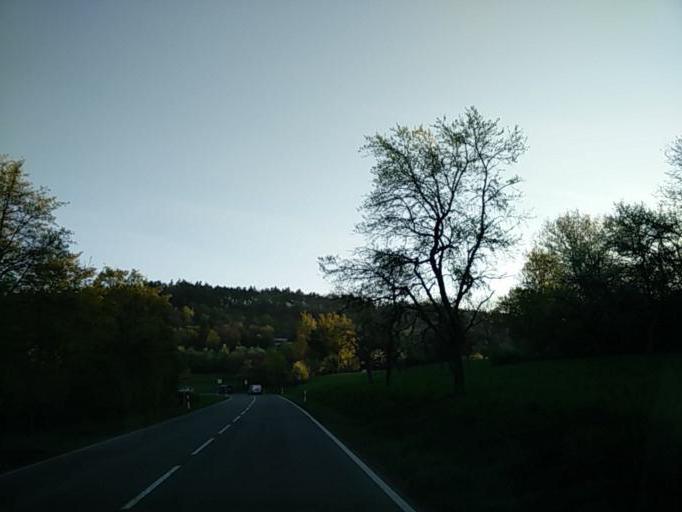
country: DE
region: Baden-Wuerttemberg
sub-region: Regierungsbezirk Stuttgart
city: Herrenberg
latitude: 48.5997
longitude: 8.8884
